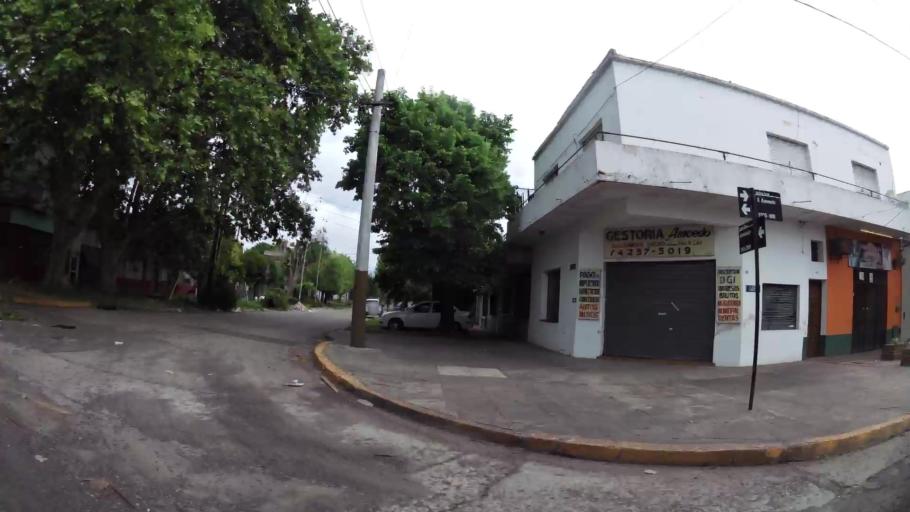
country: AR
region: Buenos Aires
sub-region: Partido de Quilmes
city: Quilmes
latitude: -34.7352
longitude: -58.2662
